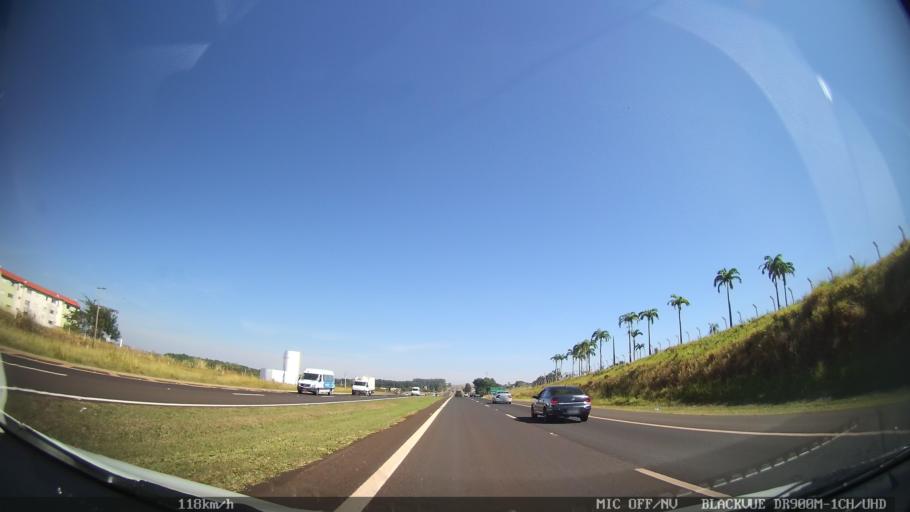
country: BR
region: Sao Paulo
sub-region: Ribeirao Preto
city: Ribeirao Preto
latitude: -21.1133
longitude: -47.8214
